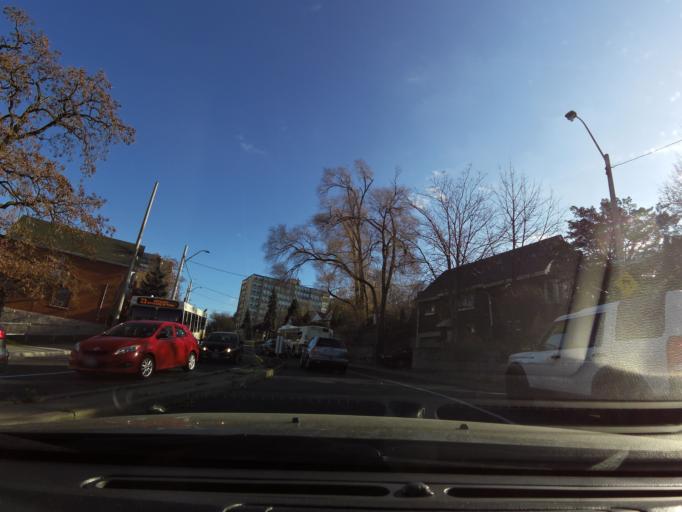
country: CA
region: Ontario
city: Hamilton
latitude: 43.2474
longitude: -79.8698
